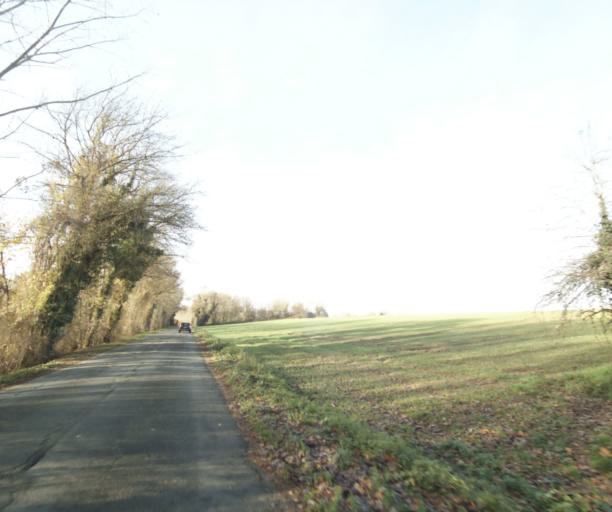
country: FR
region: Poitou-Charentes
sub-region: Departement de la Charente-Maritime
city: Chaniers
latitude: 45.7101
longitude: -0.5395
